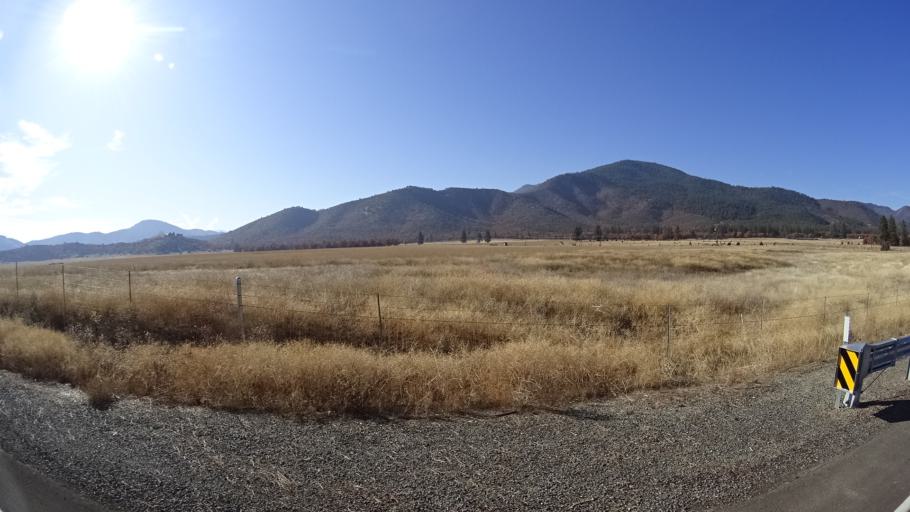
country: US
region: California
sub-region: Siskiyou County
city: Montague
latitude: 41.6560
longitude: -122.5809
